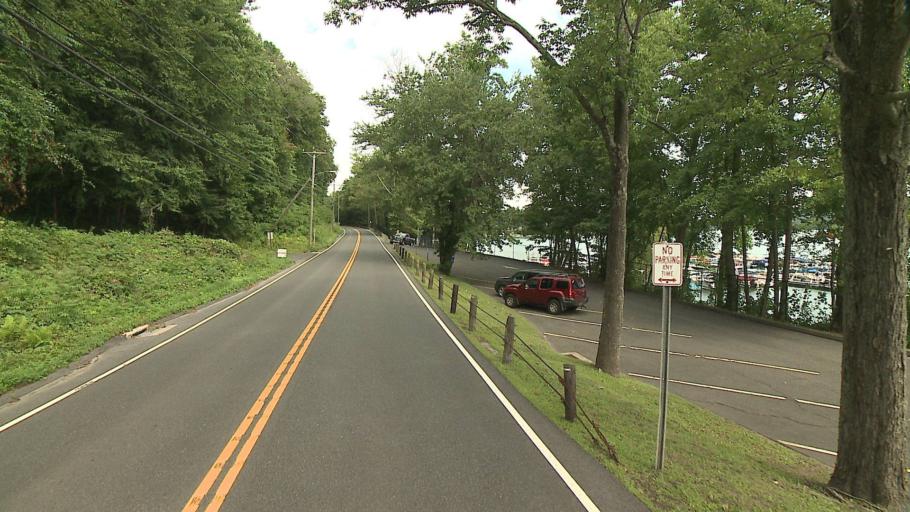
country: US
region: New York
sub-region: Putnam County
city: Putnam Lake
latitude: 41.4907
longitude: -73.4665
